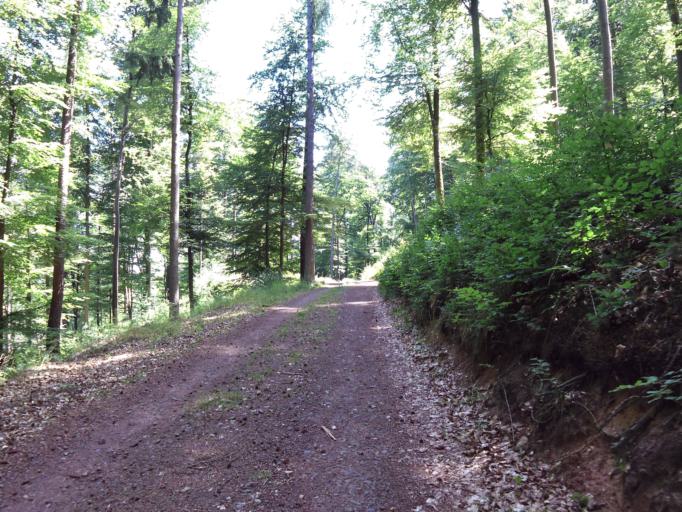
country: DE
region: Rheinland-Pfalz
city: Wilgartswiesen
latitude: 49.2683
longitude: 7.8624
